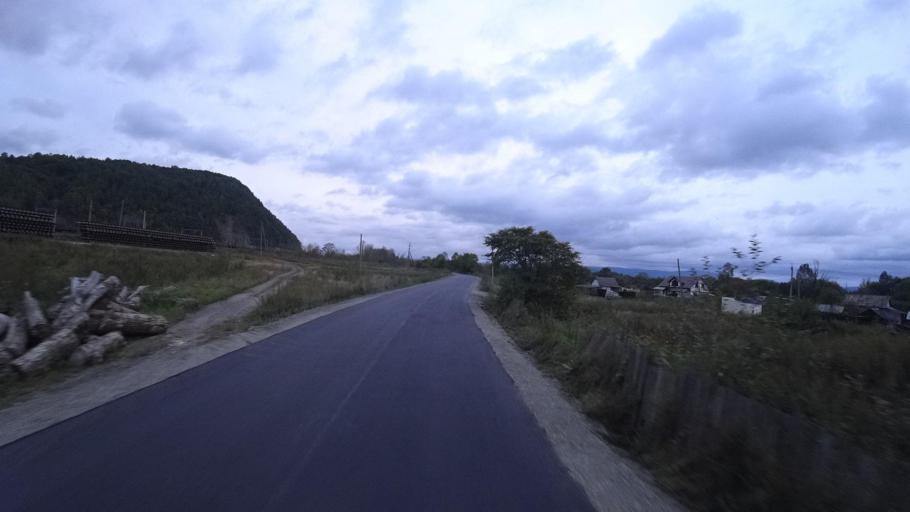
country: RU
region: Jewish Autonomous Oblast
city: Izvestkovyy
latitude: 48.9905
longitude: 131.5461
